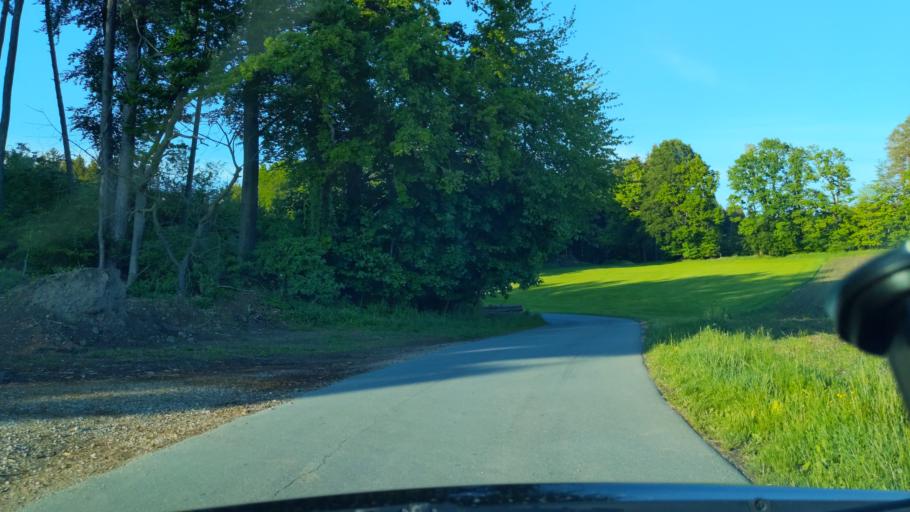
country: DE
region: Bavaria
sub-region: Upper Bavaria
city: Ebersberg
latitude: 48.0740
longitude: 11.9939
